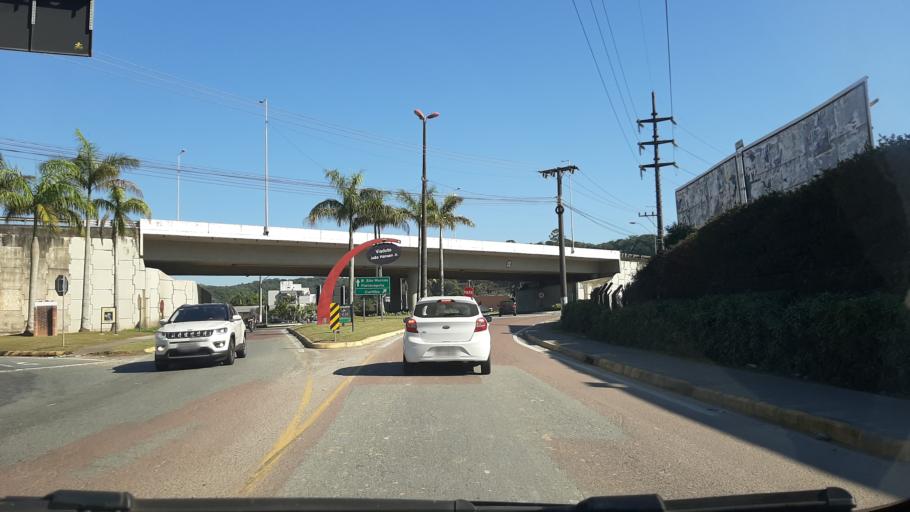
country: BR
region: Santa Catarina
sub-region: Joinville
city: Joinville
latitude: -26.3186
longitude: -48.8709
